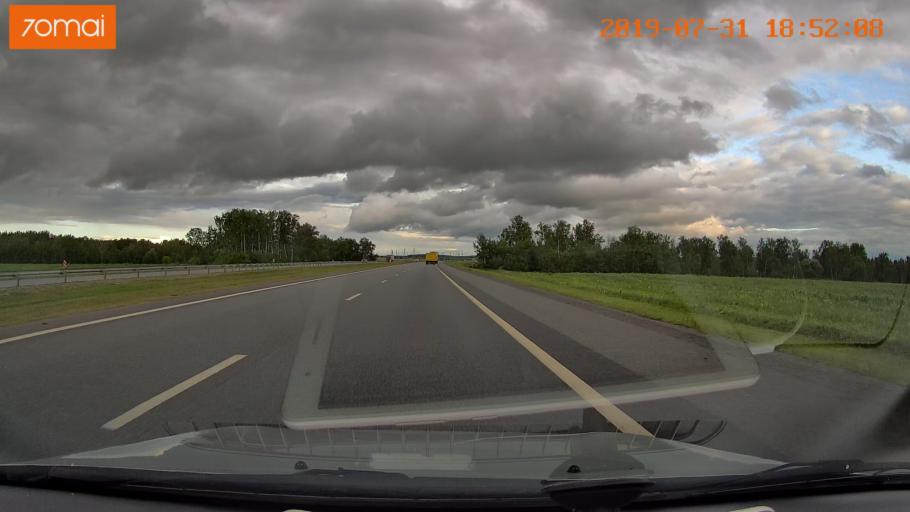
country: RU
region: Moskovskaya
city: Voskresensk
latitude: 55.2165
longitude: 38.6243
